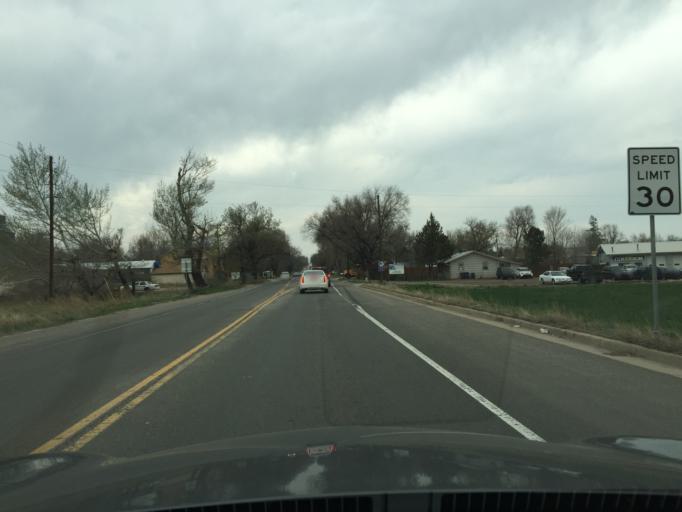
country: US
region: Colorado
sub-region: Boulder County
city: Lafayette
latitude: 40.0003
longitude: -105.0784
